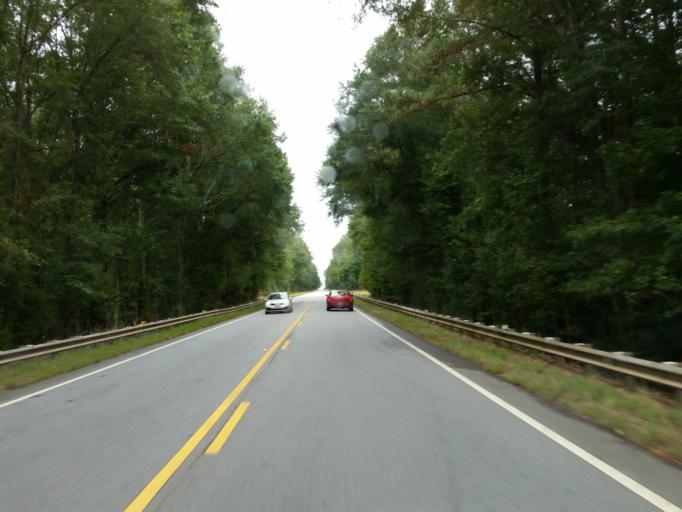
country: US
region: Georgia
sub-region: Crawford County
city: Roberta
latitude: 32.8659
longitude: -84.0863
